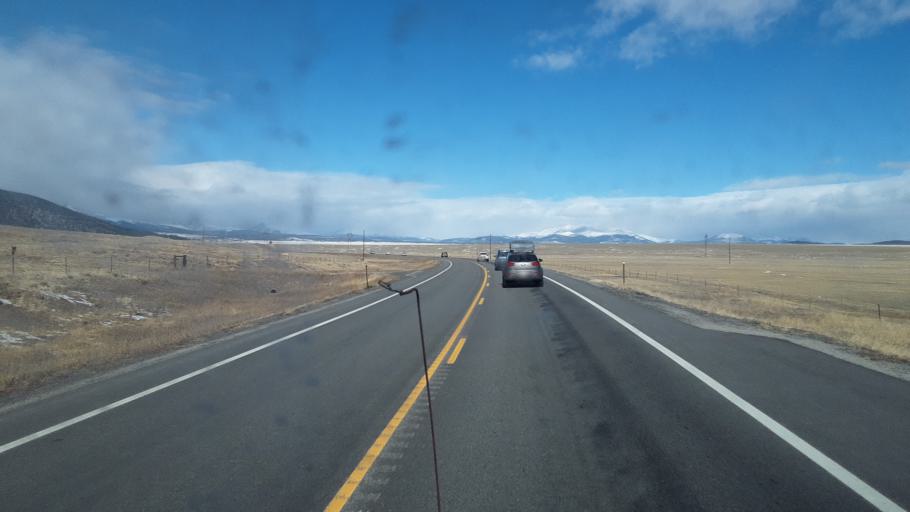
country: US
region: Colorado
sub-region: Park County
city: Fairplay
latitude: 39.0781
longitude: -105.9741
